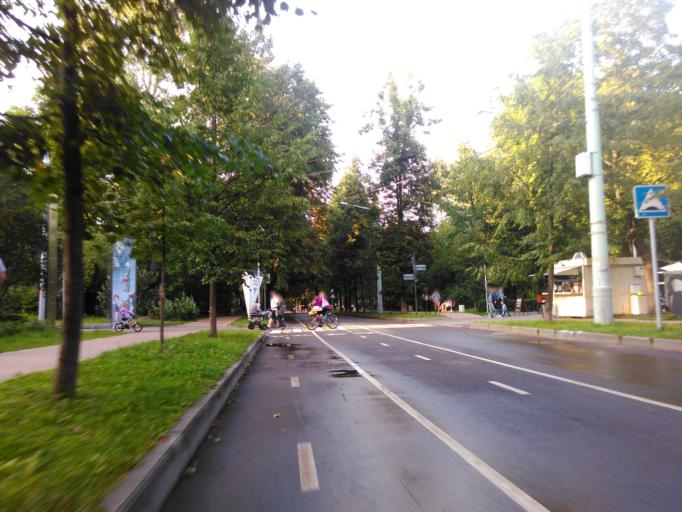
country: RU
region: Moscow
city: Sokol'niki
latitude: 55.7946
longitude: 37.6668
